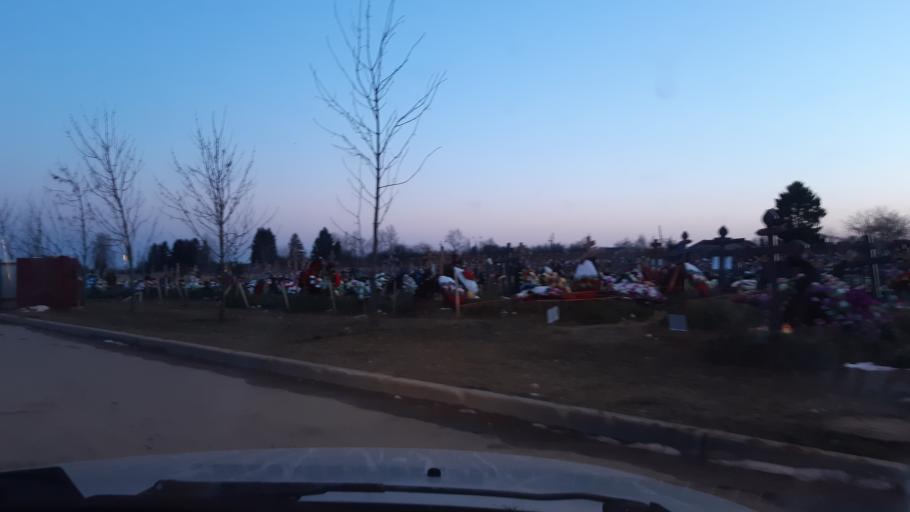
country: RU
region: Moskovskaya
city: Alabushevo
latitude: 56.0159
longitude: 37.1352
